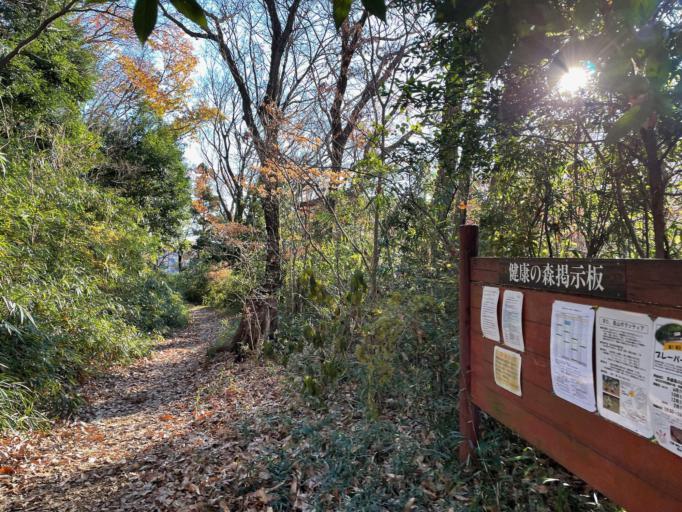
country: JP
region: Tokyo
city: Chofugaoka
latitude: 35.6207
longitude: 139.5239
